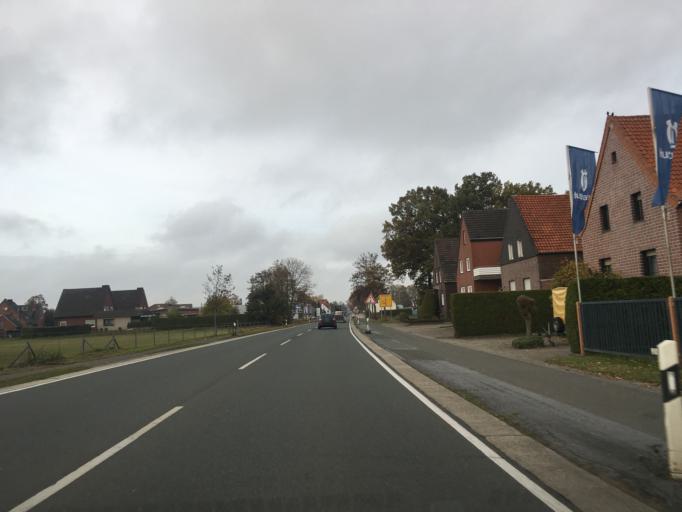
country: DE
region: North Rhine-Westphalia
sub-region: Regierungsbezirk Munster
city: Laer
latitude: 52.1027
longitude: 7.4070
